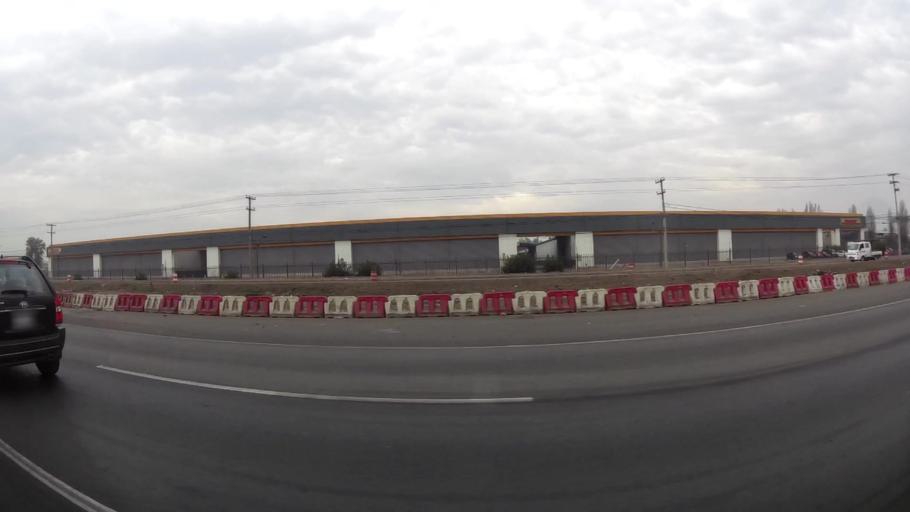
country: CL
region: Santiago Metropolitan
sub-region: Provincia de Chacabuco
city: Chicureo Abajo
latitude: -33.2934
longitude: -70.7329
